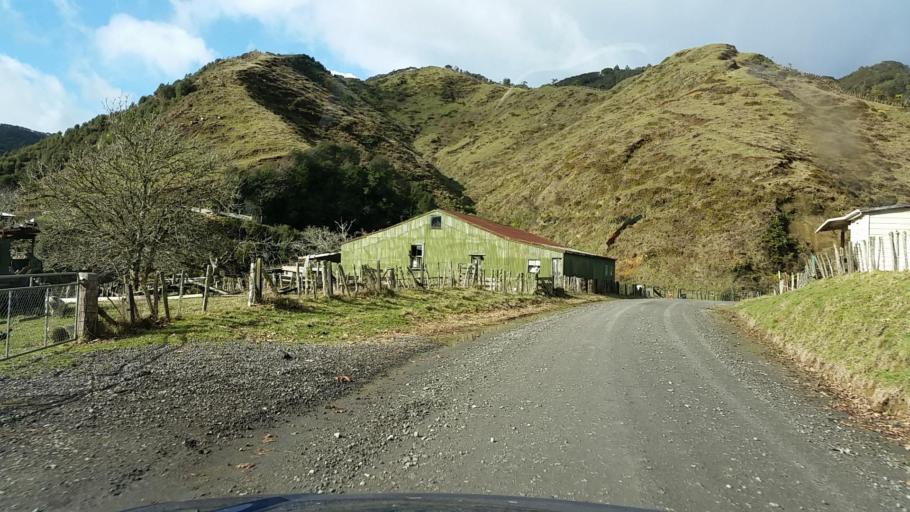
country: NZ
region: Taranaki
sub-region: South Taranaki District
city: Eltham
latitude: -39.2611
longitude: 174.7426
